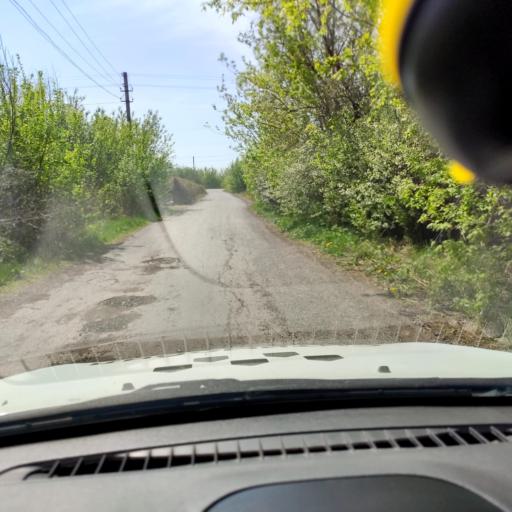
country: RU
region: Samara
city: Tol'yatti
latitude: 53.6642
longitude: 49.3622
